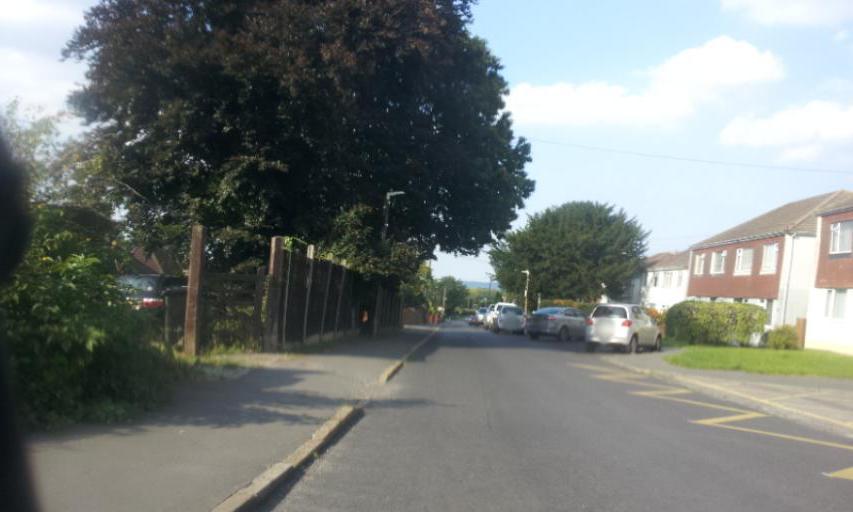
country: GB
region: England
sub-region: Kent
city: Maidstone
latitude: 51.2342
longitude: 0.4953
